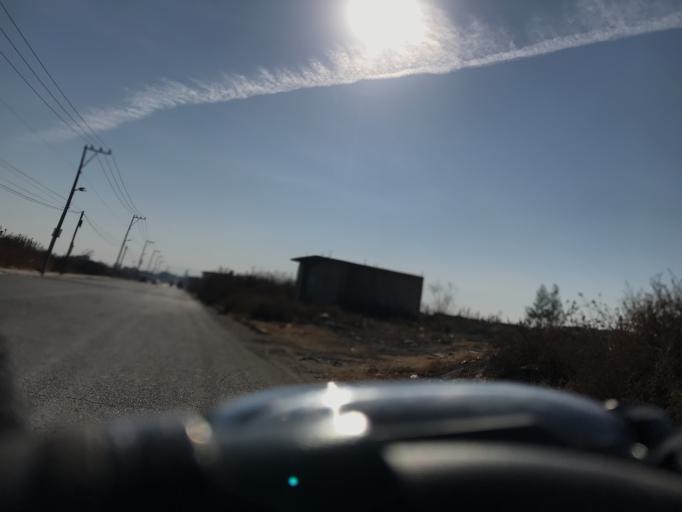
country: MX
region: Mexico
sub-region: Tonanitla
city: Colonia la Asuncion
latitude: 19.6911
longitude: -99.0600
